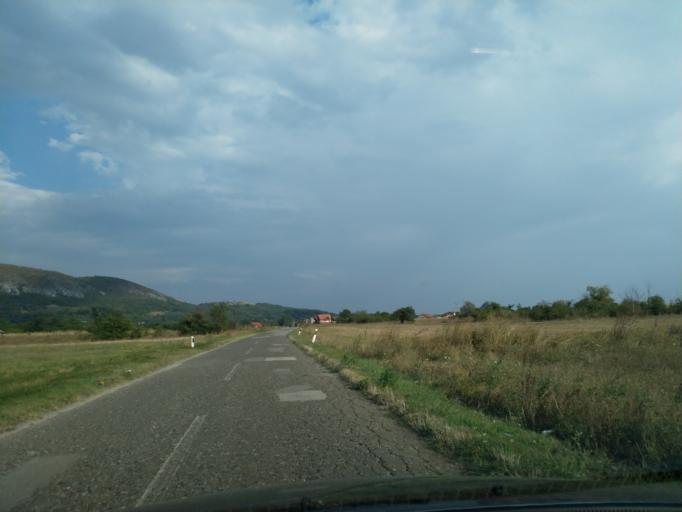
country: RS
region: Central Serbia
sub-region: Pomoravski Okrug
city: Paracin
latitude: 43.8240
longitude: 21.5318
